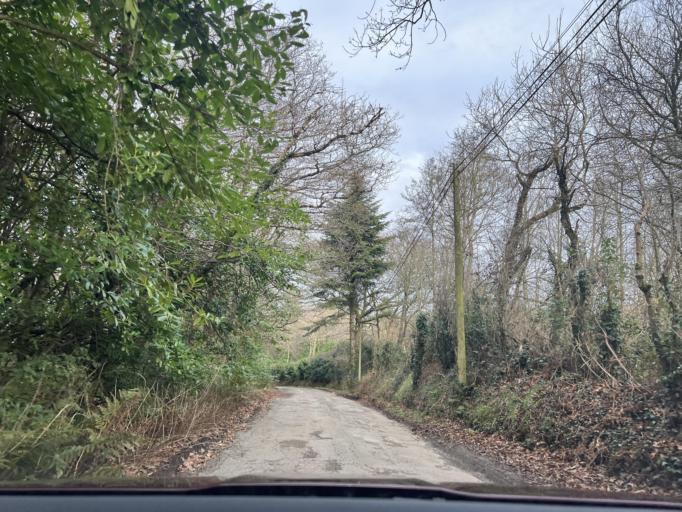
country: IE
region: Leinster
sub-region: Loch Garman
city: Loch Garman
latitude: 52.3666
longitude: -6.5325
